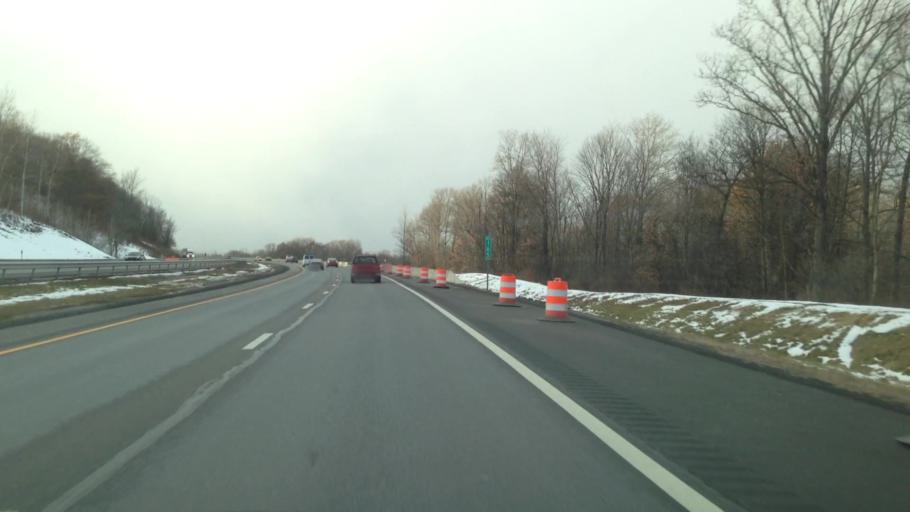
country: US
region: New York
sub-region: Schenectady County
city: Scotia
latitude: 42.8695
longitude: -74.0458
